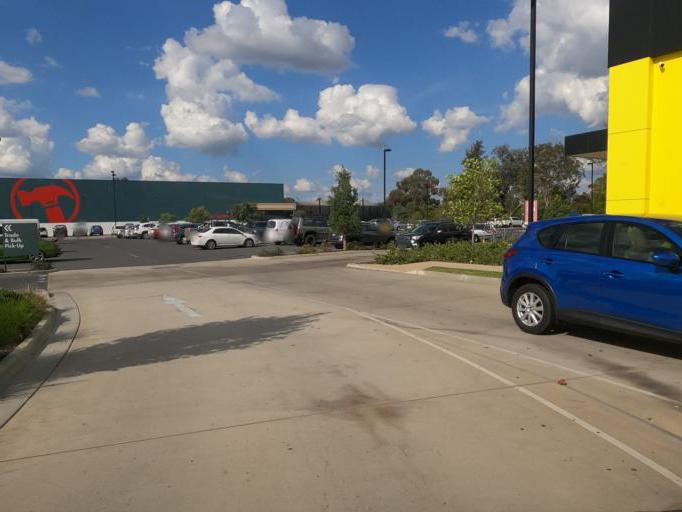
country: AU
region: New South Wales
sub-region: Albury Municipality
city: East Albury
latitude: -36.0746
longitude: 146.9481
